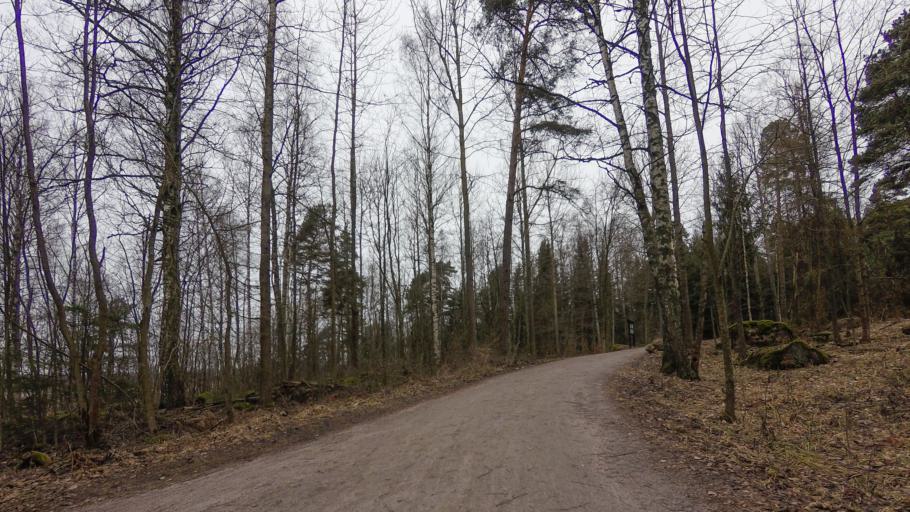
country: FI
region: Uusimaa
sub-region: Helsinki
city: Vantaa
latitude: 60.2154
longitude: 25.0098
